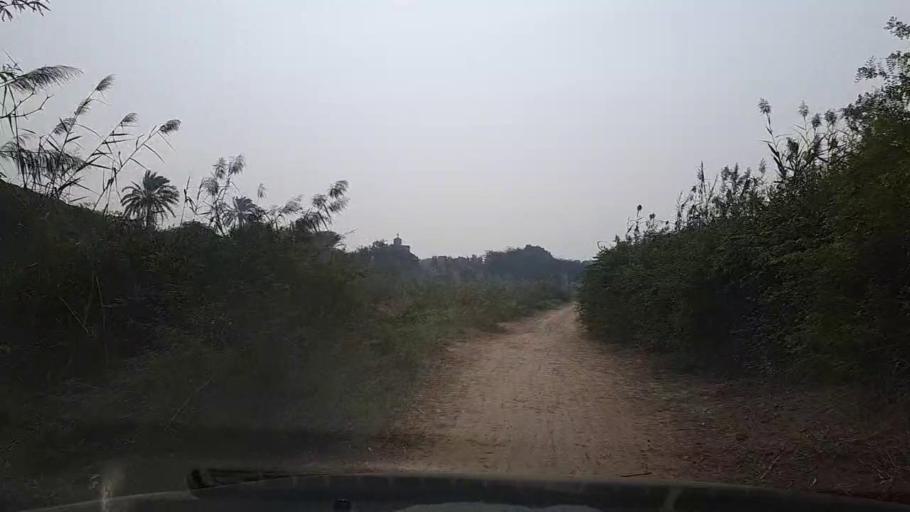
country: PK
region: Sindh
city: Thatta
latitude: 24.5534
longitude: 67.8396
